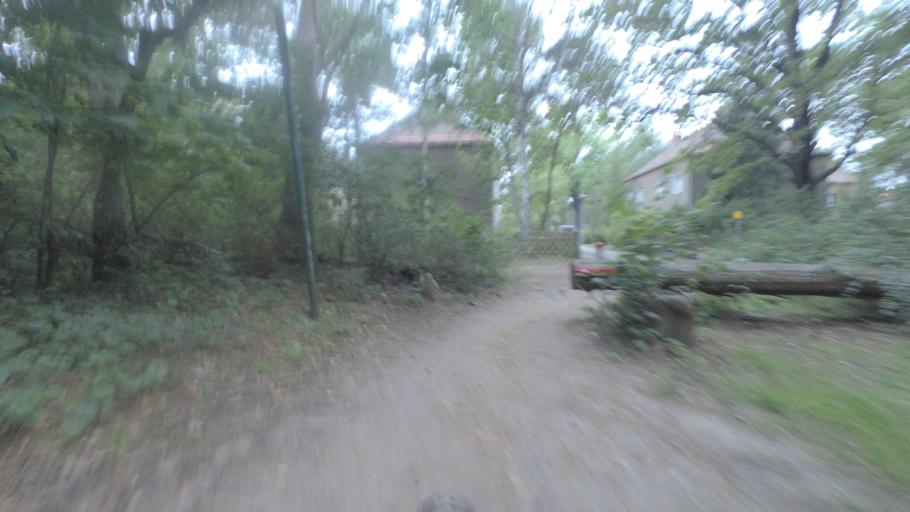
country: DE
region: Berlin
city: Berlin Koepenick
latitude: 52.4596
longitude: 13.5960
